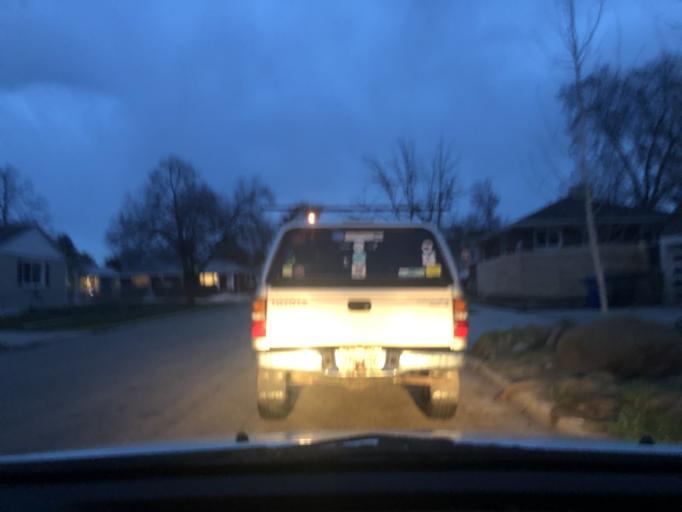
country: US
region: Utah
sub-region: Salt Lake County
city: South Salt Lake
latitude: 40.7238
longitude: -111.8746
